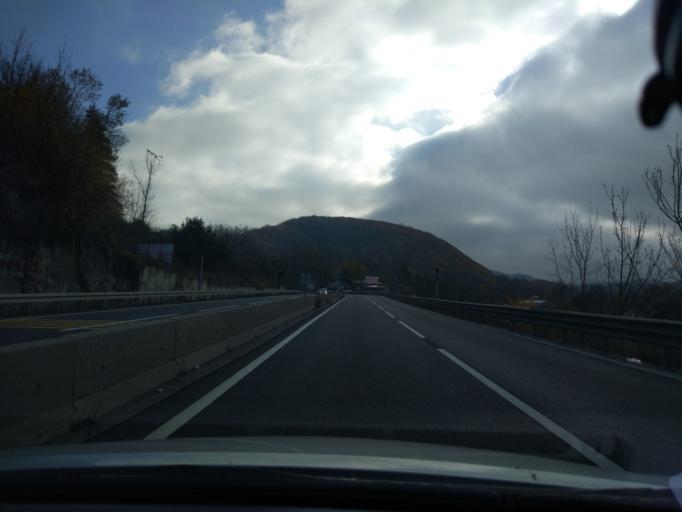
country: TR
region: Duzce
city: Kaynasli
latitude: 40.7600
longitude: 31.3491
